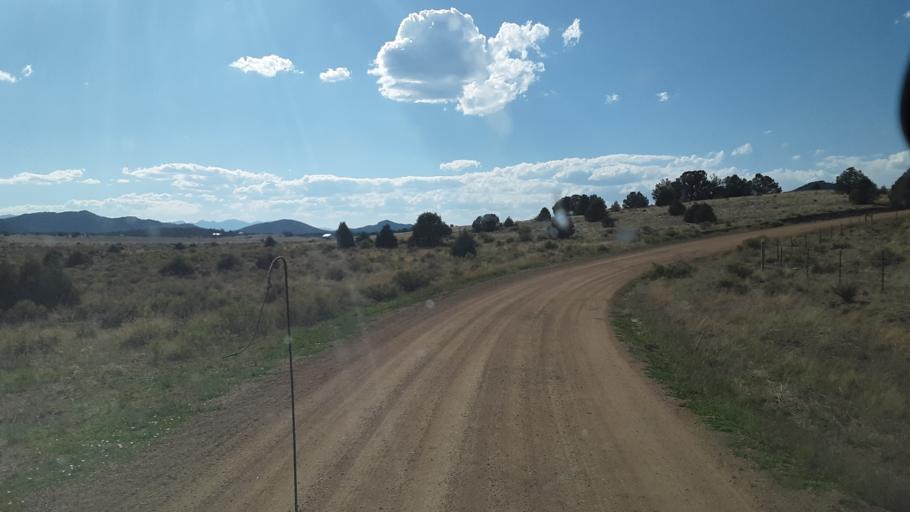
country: US
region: Colorado
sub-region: Custer County
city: Westcliffe
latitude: 38.2845
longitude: -105.4769
